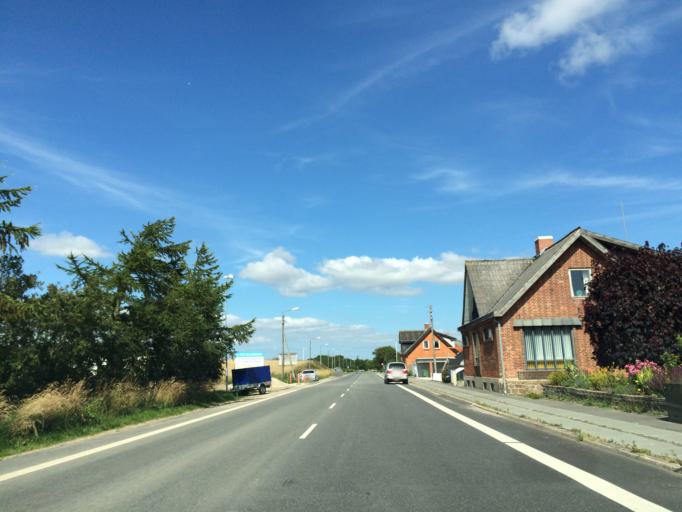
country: DK
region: Central Jutland
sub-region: Arhus Kommune
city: Logten
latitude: 56.2814
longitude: 10.3216
